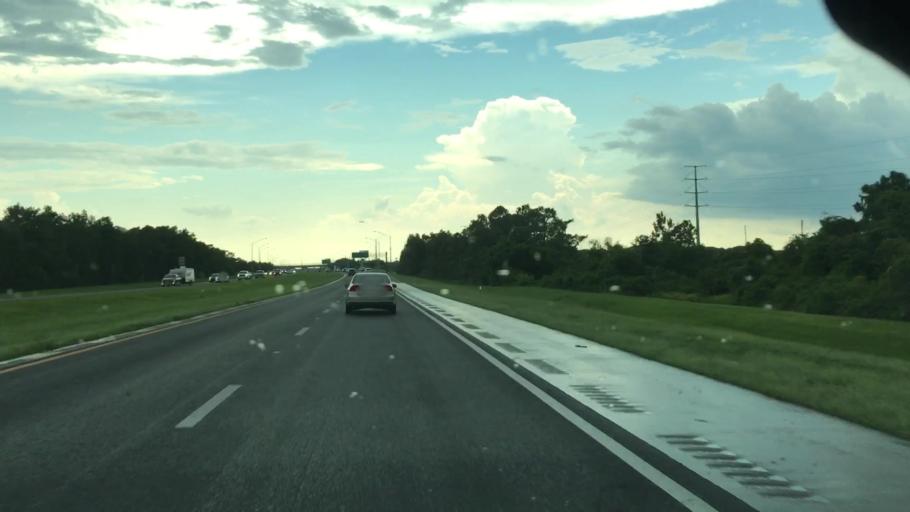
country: US
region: Florida
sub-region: Osceola County
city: Buenaventura Lakes
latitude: 28.3832
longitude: -81.2666
